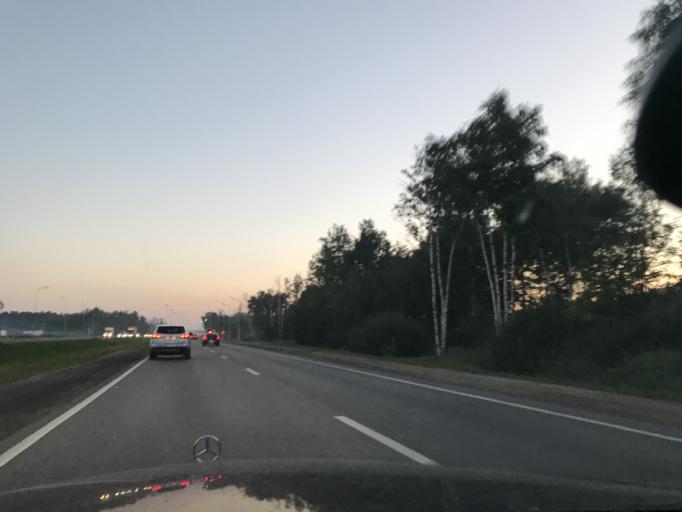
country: RU
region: Moskovskaya
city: Noginsk
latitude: 55.8456
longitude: 38.4879
